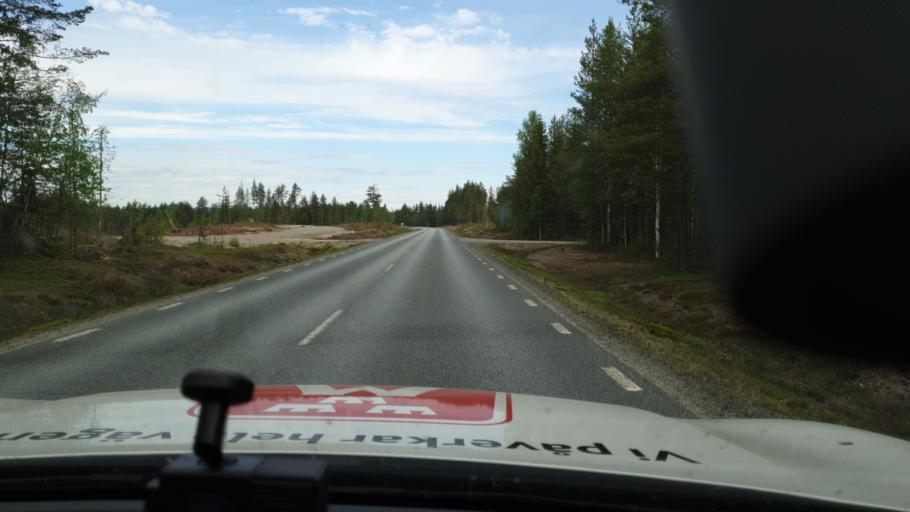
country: SE
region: Vaesterbotten
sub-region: Mala Kommun
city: Mala
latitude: 65.0522
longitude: 18.3918
